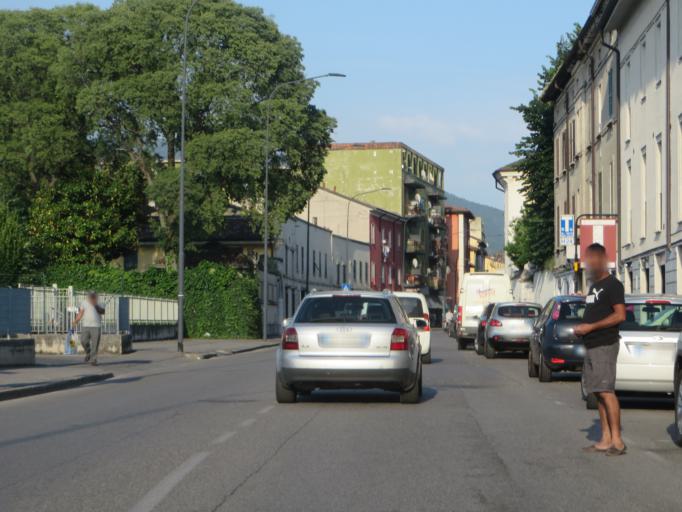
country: IT
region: Lombardy
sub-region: Provincia di Brescia
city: Brescia
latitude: 45.5462
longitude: 10.1895
